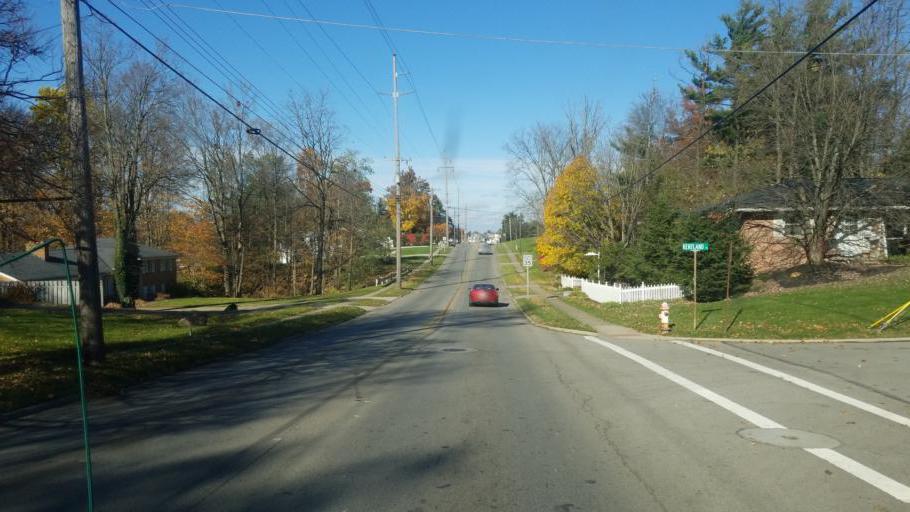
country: US
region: Ohio
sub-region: Richland County
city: Mansfield
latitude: 40.7557
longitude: -82.5517
